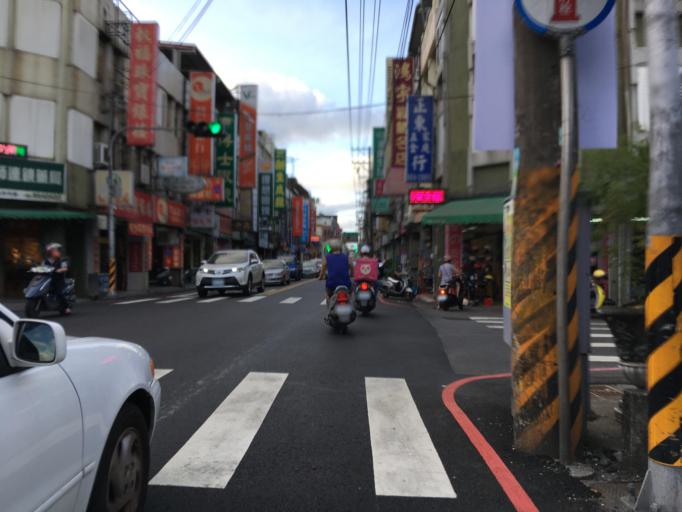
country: TW
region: Taiwan
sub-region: Yilan
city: Yilan
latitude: 24.6735
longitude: 121.7706
